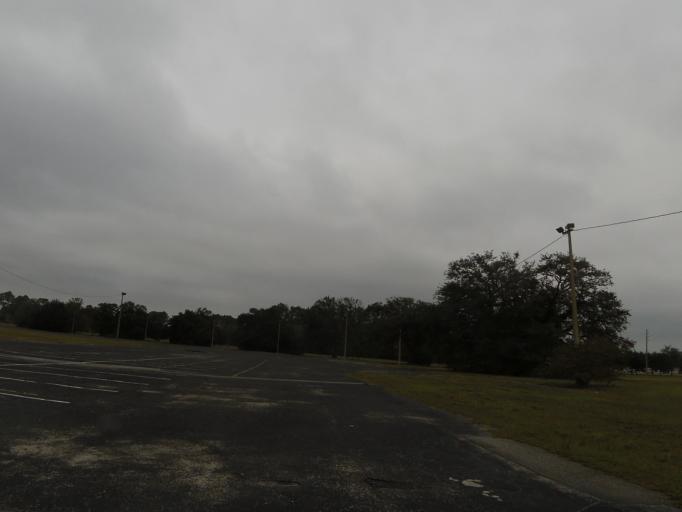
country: US
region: Florida
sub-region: Duval County
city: Baldwin
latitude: 30.2285
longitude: -81.8845
